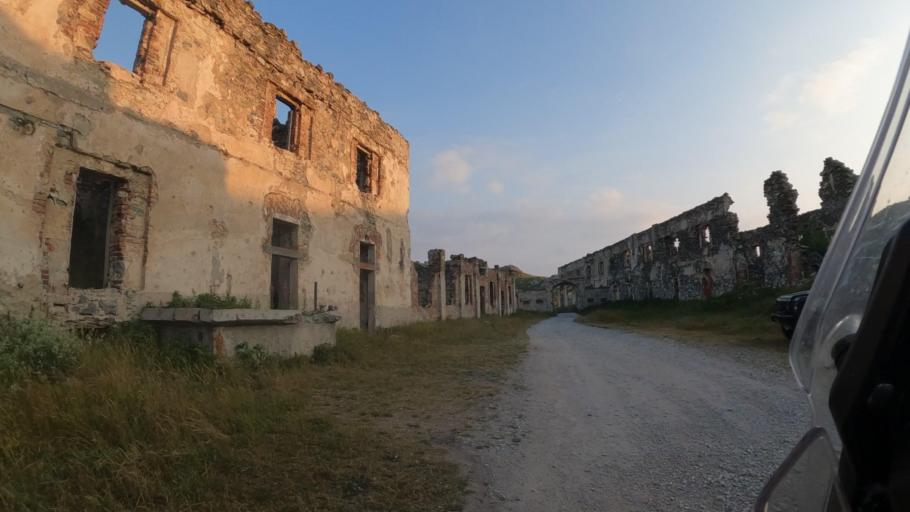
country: IT
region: Piedmont
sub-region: Provincia di Cuneo
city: Limone Piemonte
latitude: 44.1518
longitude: 7.5674
